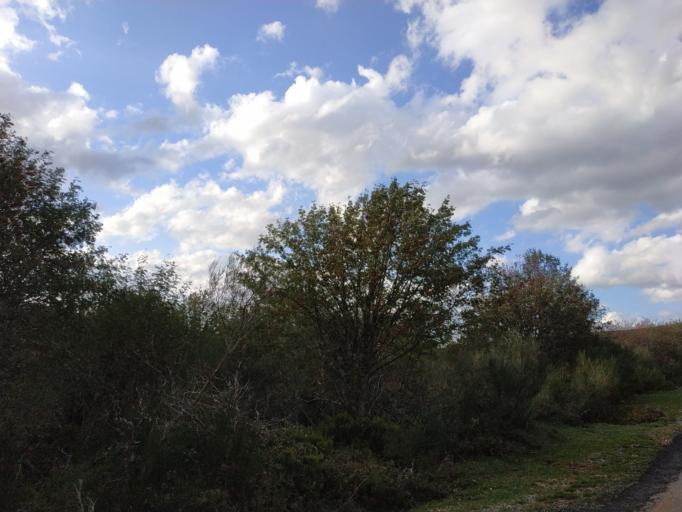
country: ES
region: Castille and Leon
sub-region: Provincia de Leon
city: Candin
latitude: 42.8767
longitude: -6.8310
